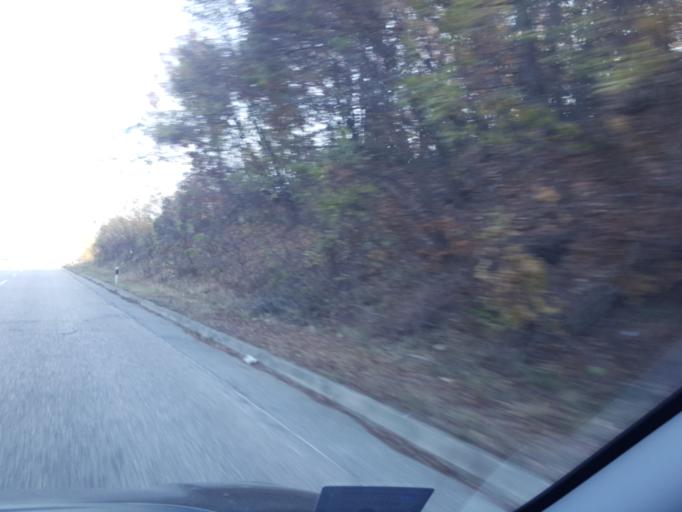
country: RS
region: Central Serbia
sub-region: Borski Okrug
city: Negotin
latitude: 44.2151
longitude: 22.4917
